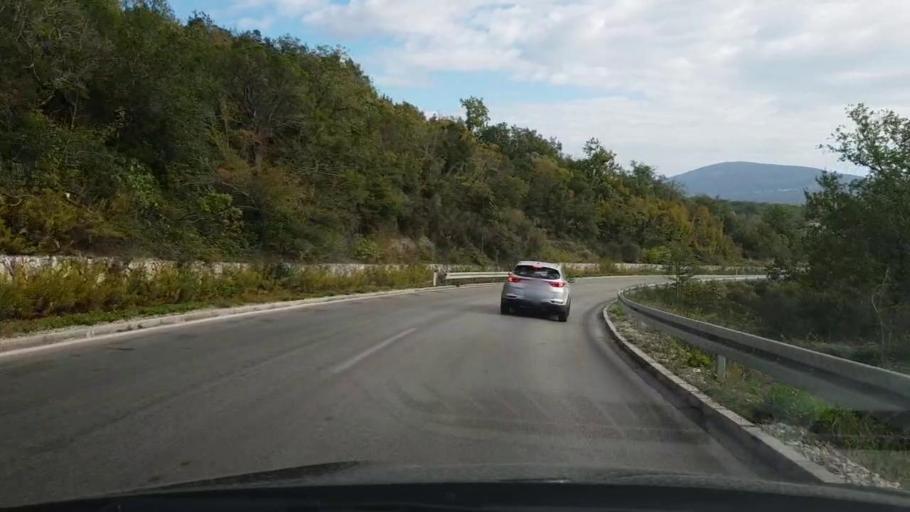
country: ME
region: Herceg Novi
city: Herceg-Novi
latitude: 42.4661
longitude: 18.5440
